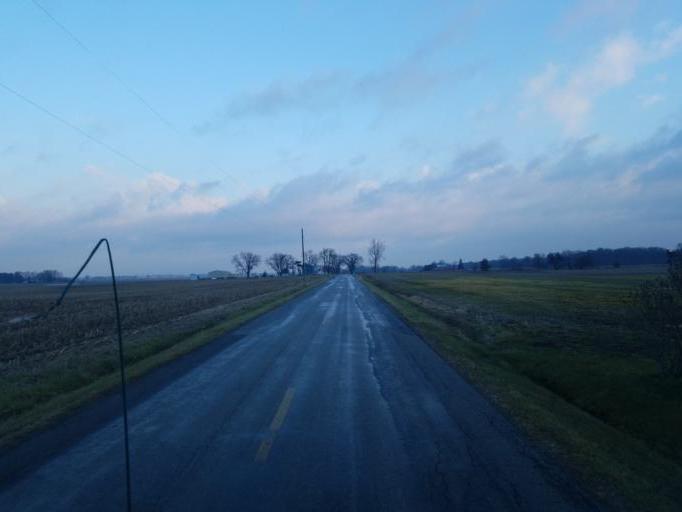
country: US
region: Ohio
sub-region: Marion County
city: Marion
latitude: 40.6375
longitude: -83.1885
